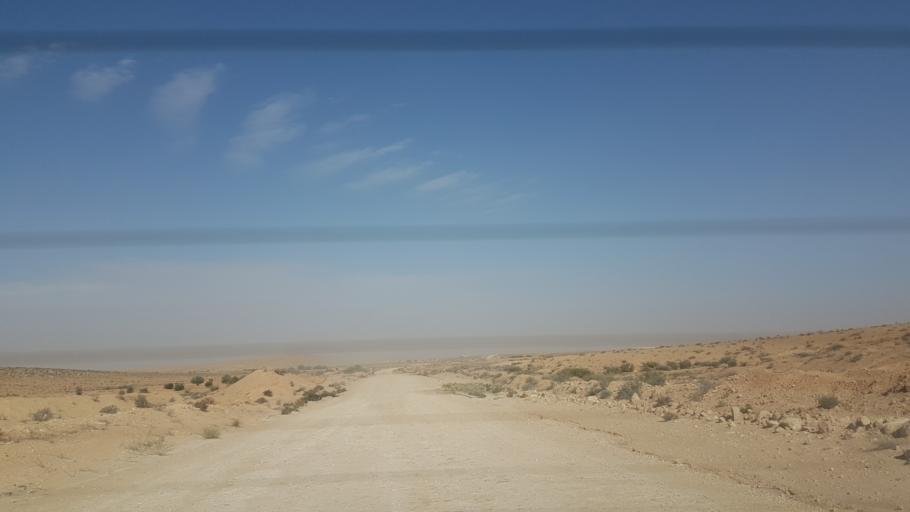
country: TN
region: Qabis
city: El Hamma
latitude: 33.6603
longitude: 9.7347
